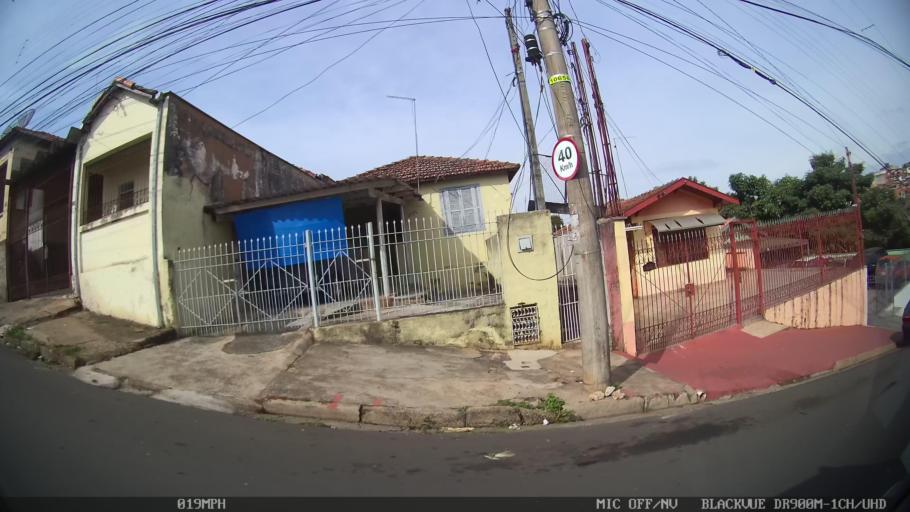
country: BR
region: Sao Paulo
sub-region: Piracicaba
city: Piracicaba
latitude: -22.7446
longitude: -47.6560
